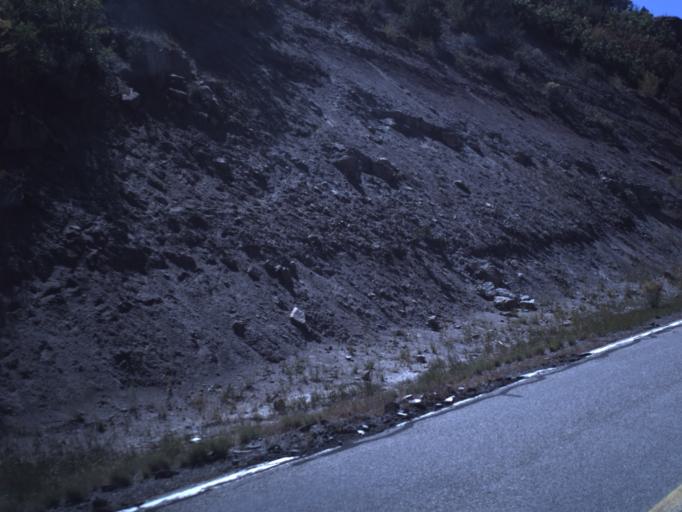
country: US
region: Utah
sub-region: Grand County
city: Moab
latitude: 38.3271
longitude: -109.1216
